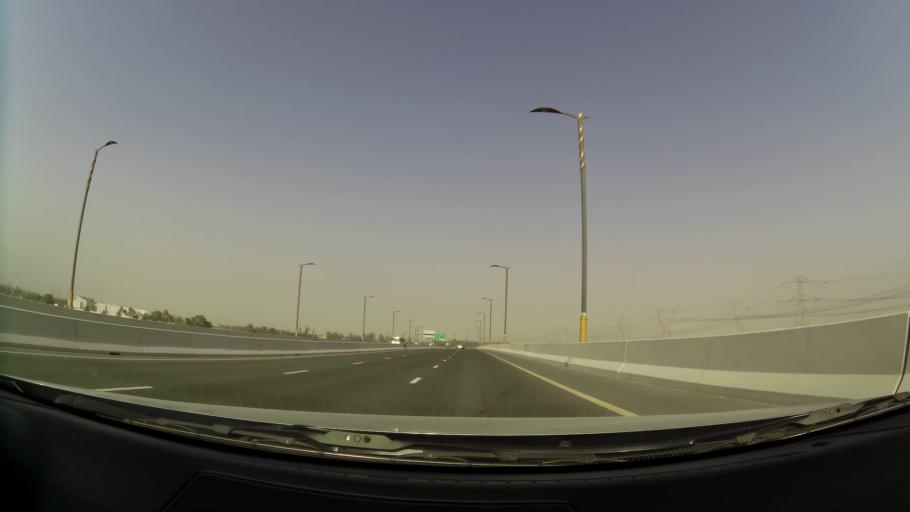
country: AE
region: Dubai
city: Dubai
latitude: 25.1707
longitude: 55.3135
